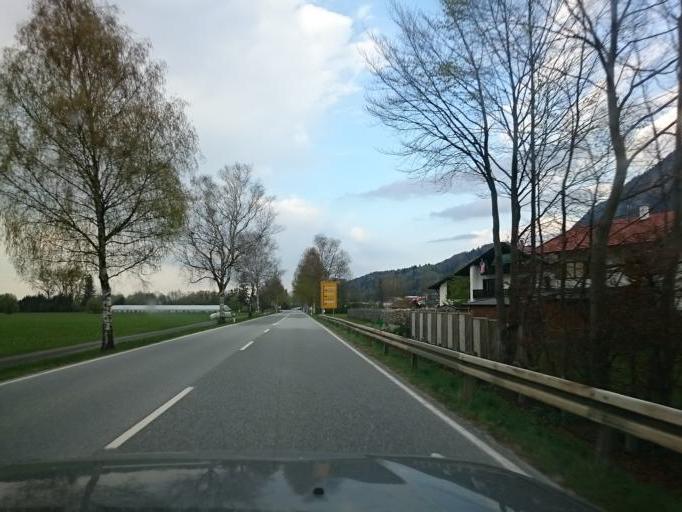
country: DE
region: Bavaria
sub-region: Upper Bavaria
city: Eschenlohe
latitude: 47.6037
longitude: 11.1870
